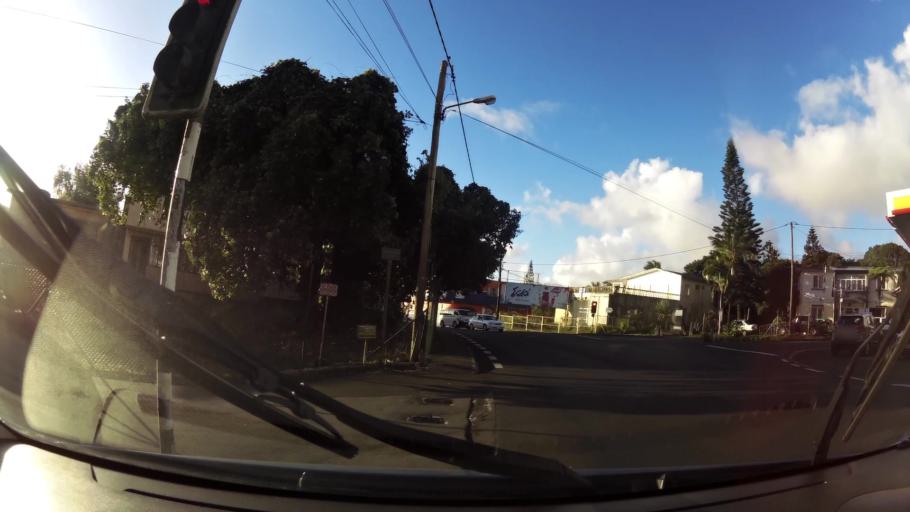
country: MU
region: Plaines Wilhems
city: Curepipe
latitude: -20.3069
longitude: 57.5255
